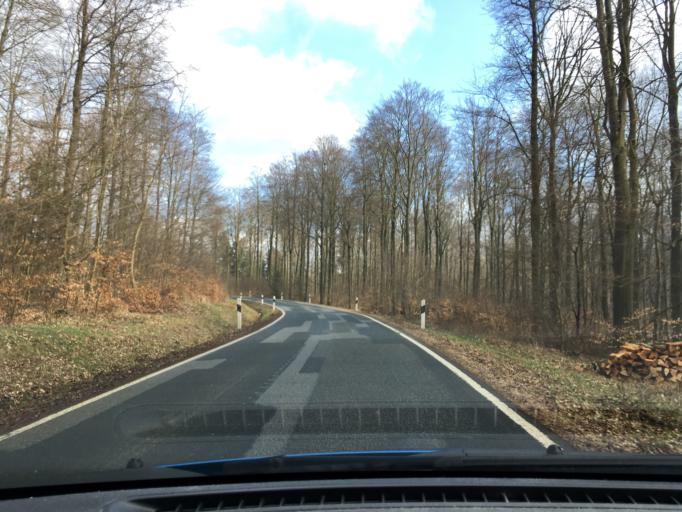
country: DE
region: Lower Saxony
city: Buhren
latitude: 51.4988
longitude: 9.6445
